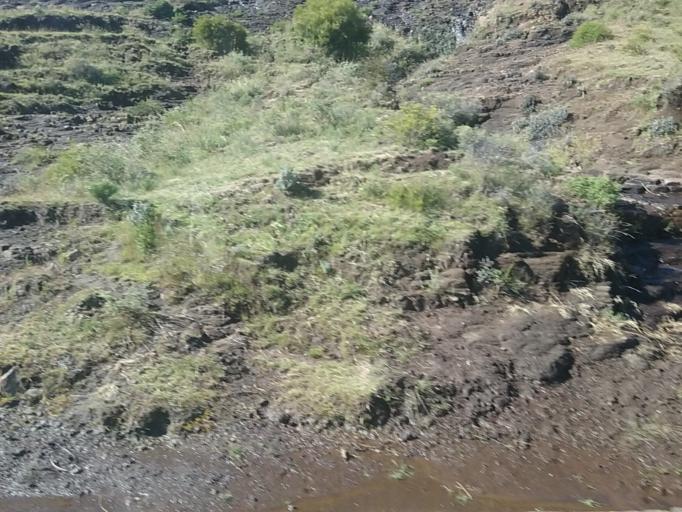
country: LS
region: Berea
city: Teyateyaneng
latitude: -29.2368
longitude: 27.9125
